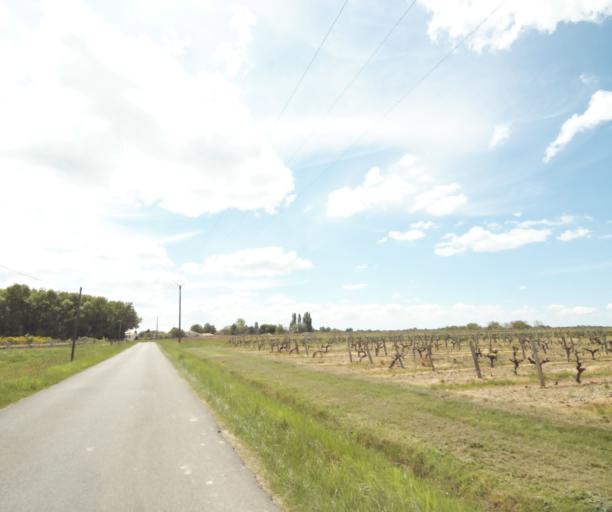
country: FR
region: Poitou-Charentes
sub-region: Departement de la Charente-Maritime
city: Burie
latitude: 45.7516
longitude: -0.4452
